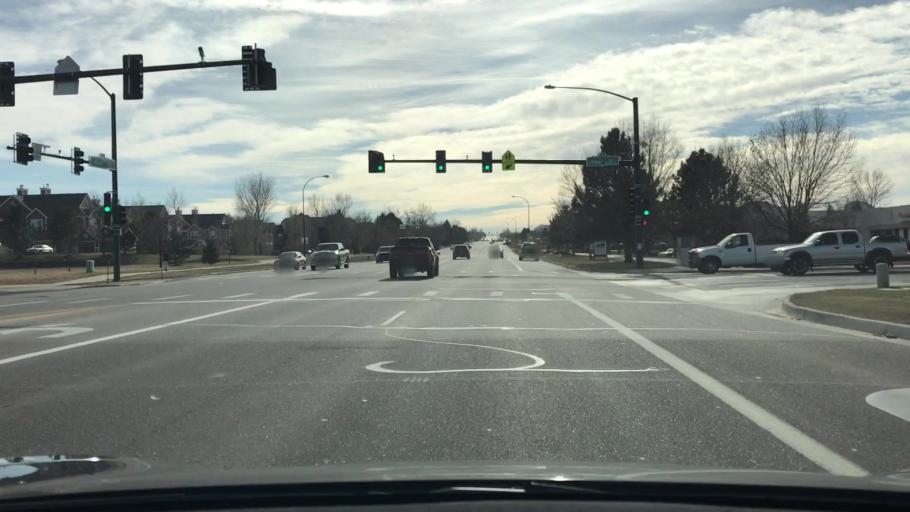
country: US
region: Colorado
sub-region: Adams County
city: Northglenn
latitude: 39.9223
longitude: -104.9969
